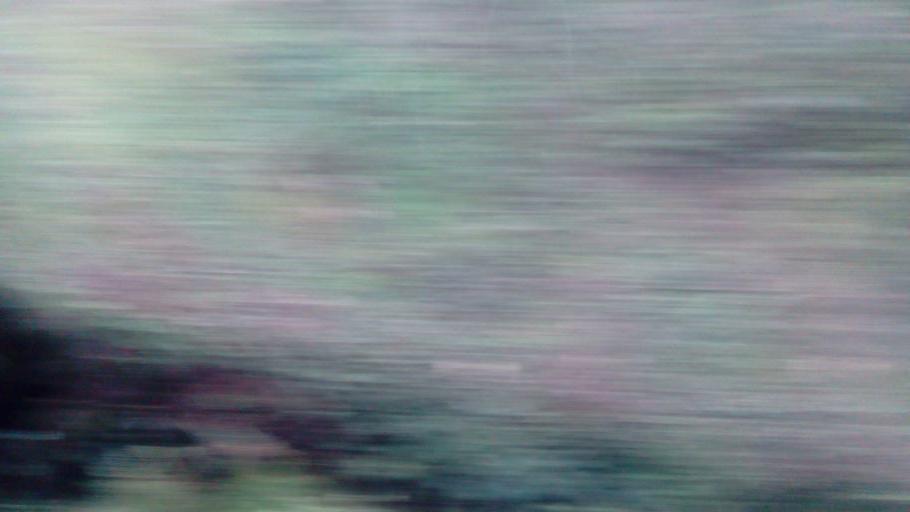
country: TW
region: Taiwan
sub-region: Yilan
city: Yilan
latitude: 24.5430
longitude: 121.4576
